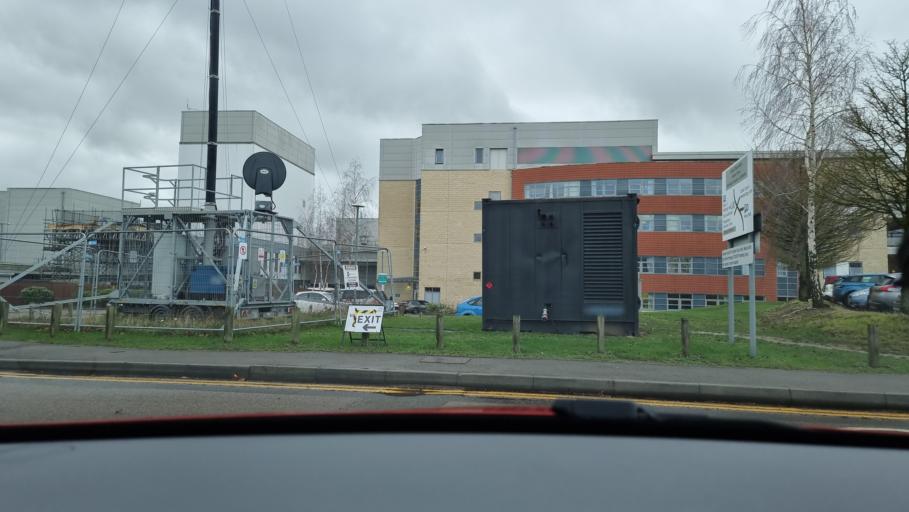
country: GB
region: England
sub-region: Buckinghamshire
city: Aylesbury
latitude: 51.7993
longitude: -0.8002
